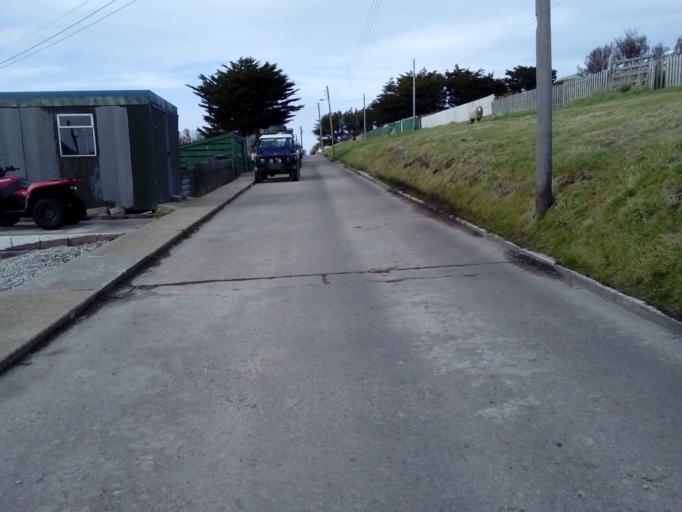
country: FK
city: Stanley
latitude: -51.6931
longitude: -57.8686
